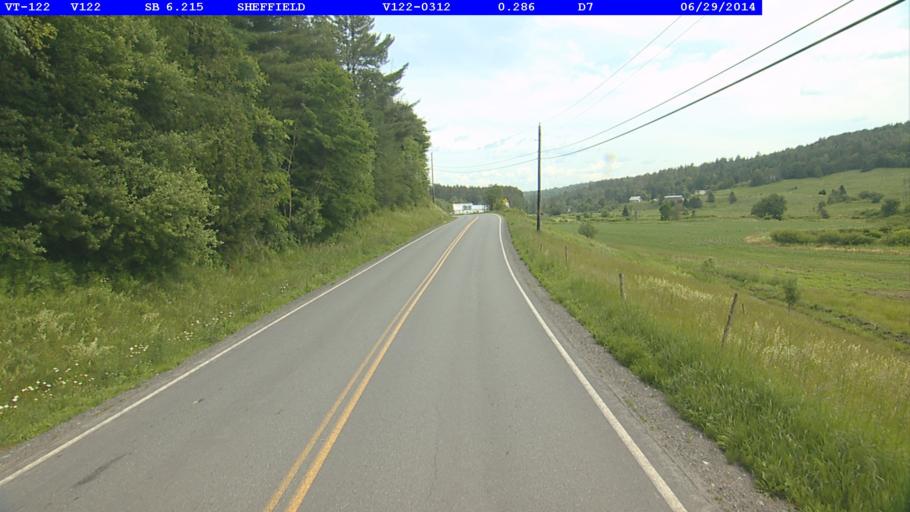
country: US
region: Vermont
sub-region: Caledonia County
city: Lyndonville
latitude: 44.5930
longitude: -72.0962
